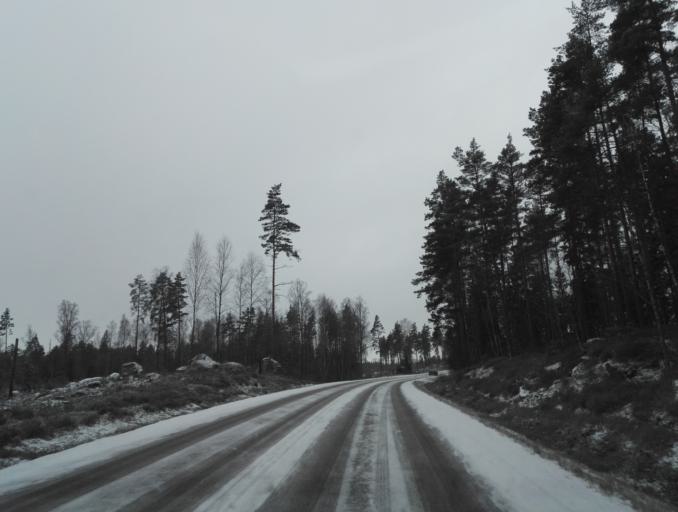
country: SE
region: Kronoberg
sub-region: Lessebo Kommun
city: Lessebo
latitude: 56.8032
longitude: 15.3494
